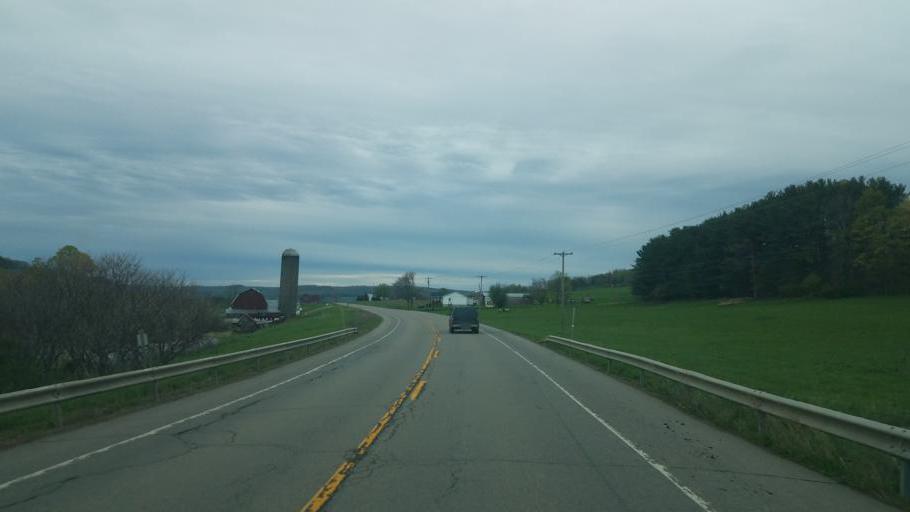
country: US
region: New York
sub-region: Steuben County
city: Canisteo
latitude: 42.1538
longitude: -77.5198
